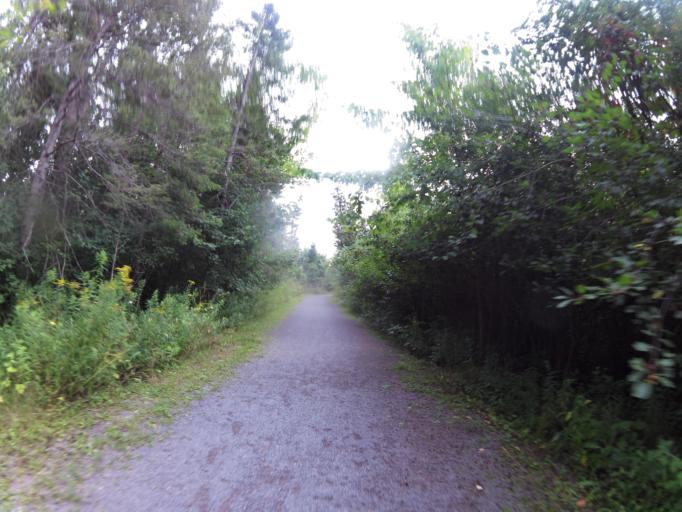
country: CA
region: Ontario
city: Bells Corners
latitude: 45.2756
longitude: -75.9365
